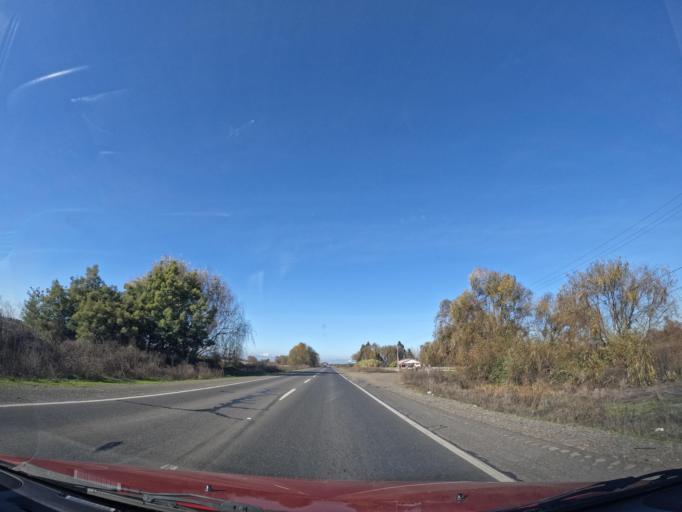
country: CL
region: Maule
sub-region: Provincia de Linares
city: San Javier
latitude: -35.6299
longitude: -71.7250
